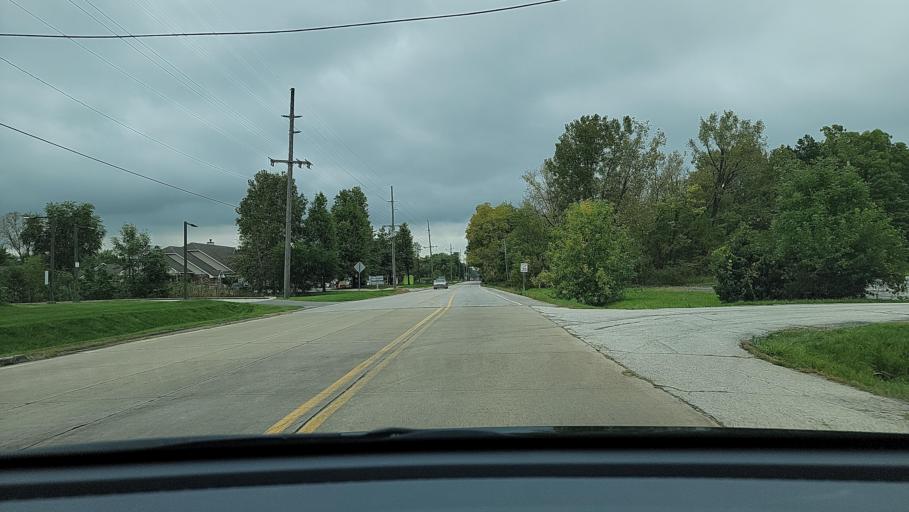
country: US
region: Indiana
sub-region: Porter County
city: Portage
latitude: 41.5512
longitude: -87.1971
